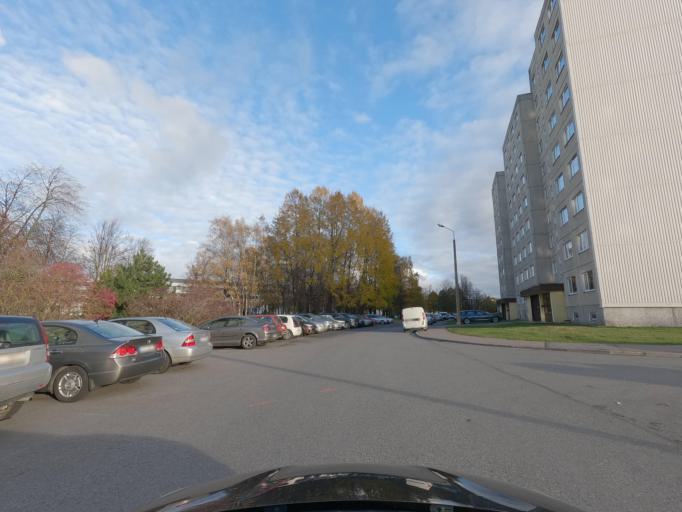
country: EE
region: Harju
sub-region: Saue vald
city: Laagri
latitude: 59.4187
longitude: 24.6475
